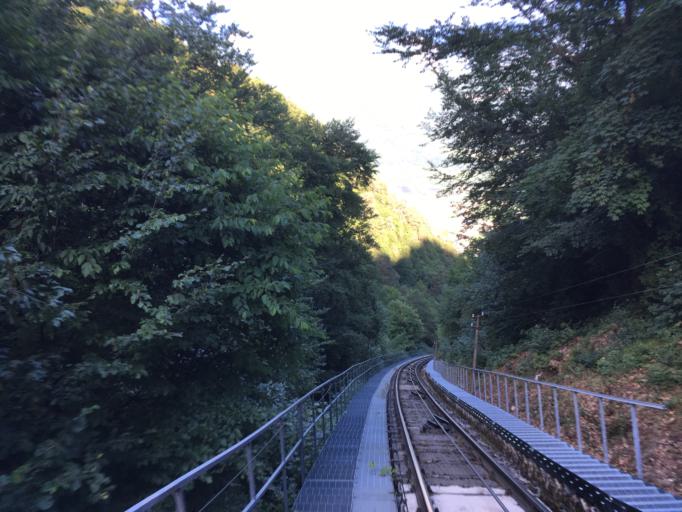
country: IT
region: Trentino-Alto Adige
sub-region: Provincia di Trento
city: Ruffre
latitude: 46.4157
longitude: 11.2119
